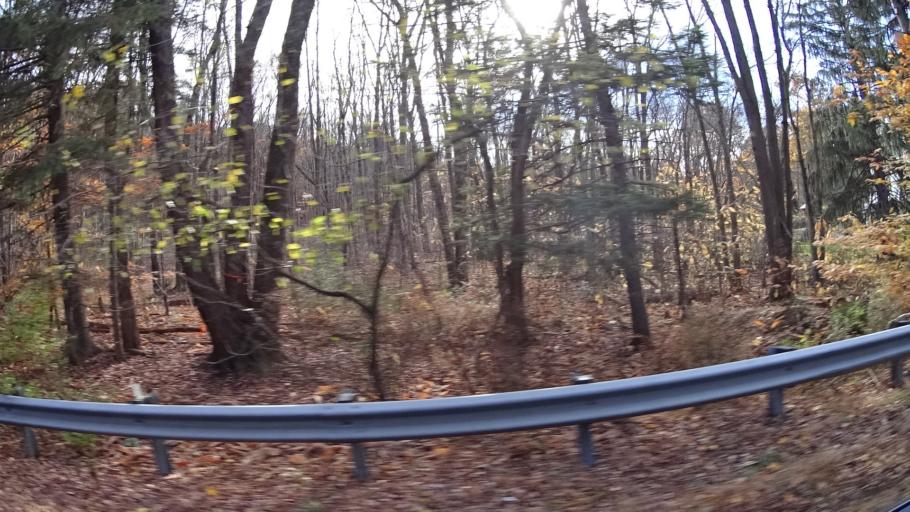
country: US
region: New Jersey
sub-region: Morris County
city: Mendham
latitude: 40.7674
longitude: -74.5613
